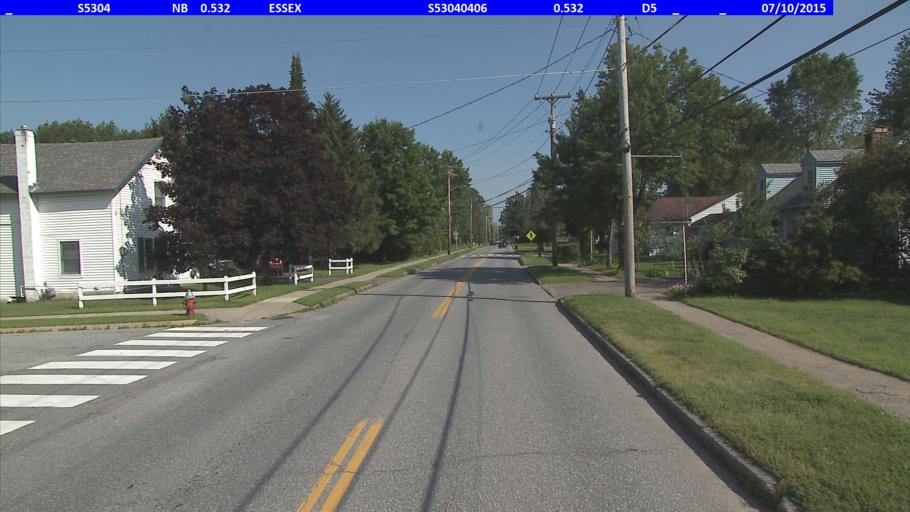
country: US
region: Vermont
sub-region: Chittenden County
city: Essex Junction
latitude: 44.4926
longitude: -73.1265
